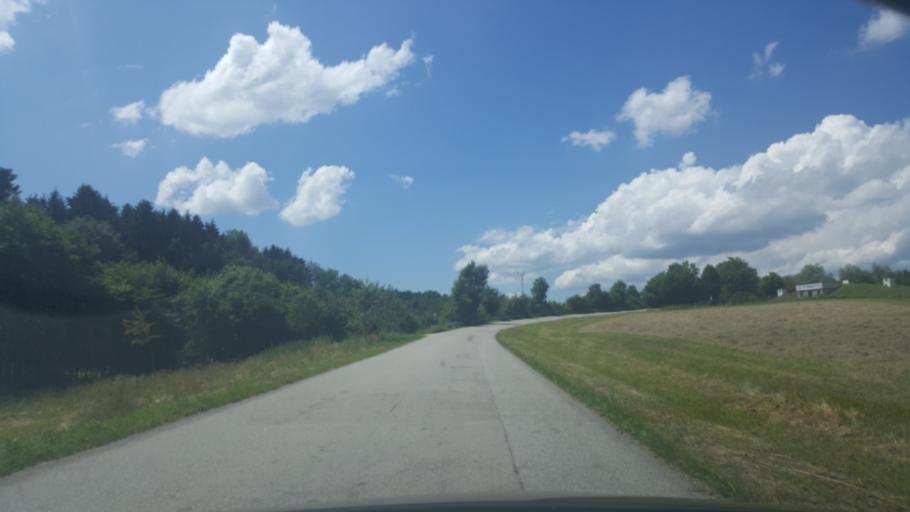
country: AT
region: Upper Austria
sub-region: Politischer Bezirk Vocklabruck
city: Seewalchen
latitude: 47.9565
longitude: 13.5778
